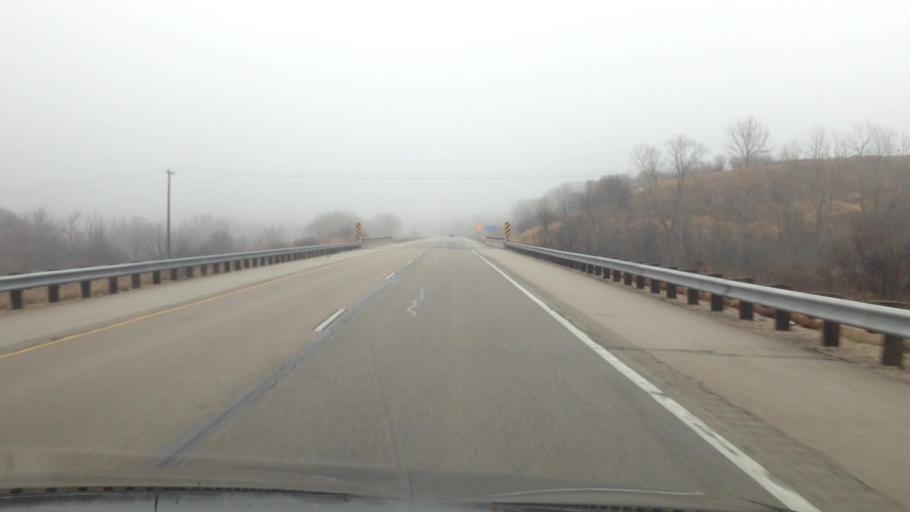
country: US
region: Wisconsin
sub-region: Walworth County
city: Elkhorn
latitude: 42.7174
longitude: -88.4717
